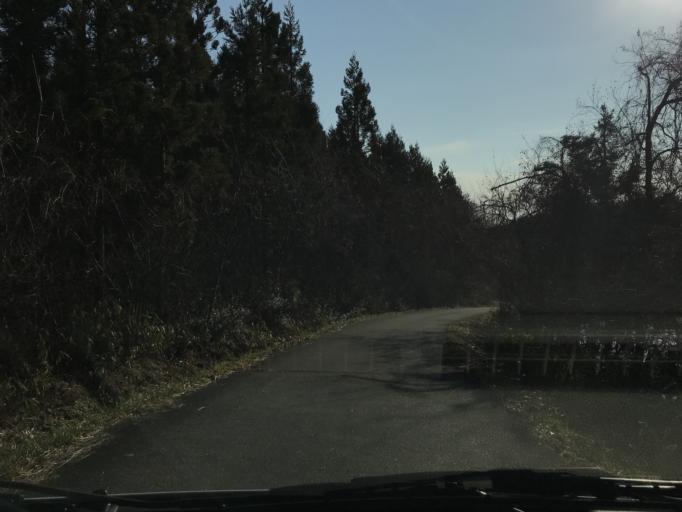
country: JP
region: Iwate
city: Ichinoseki
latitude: 38.9745
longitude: 141.0453
